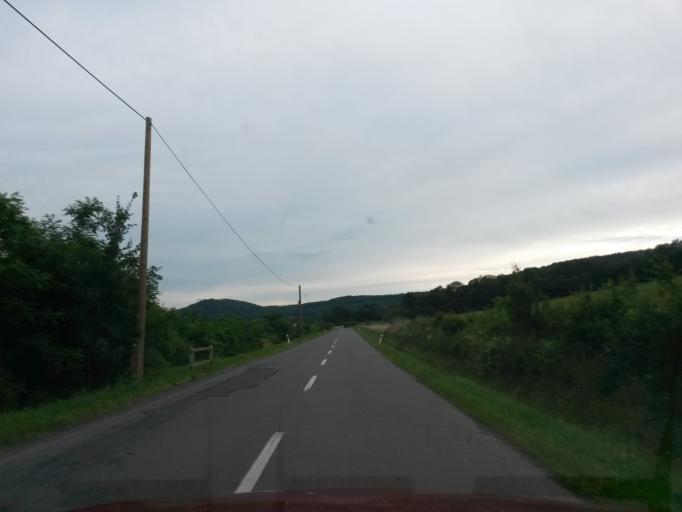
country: SK
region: Banskobystricky
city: Velky Krtis
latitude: 48.3168
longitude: 19.4029
